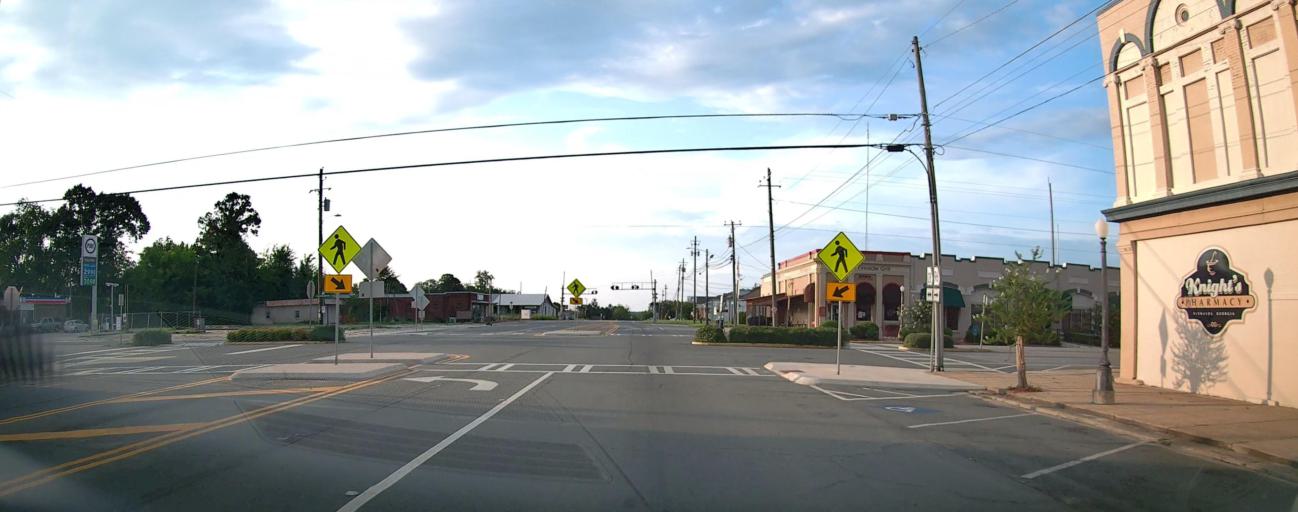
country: US
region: Georgia
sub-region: Taylor County
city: Reynolds
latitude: 32.5595
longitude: -84.0962
